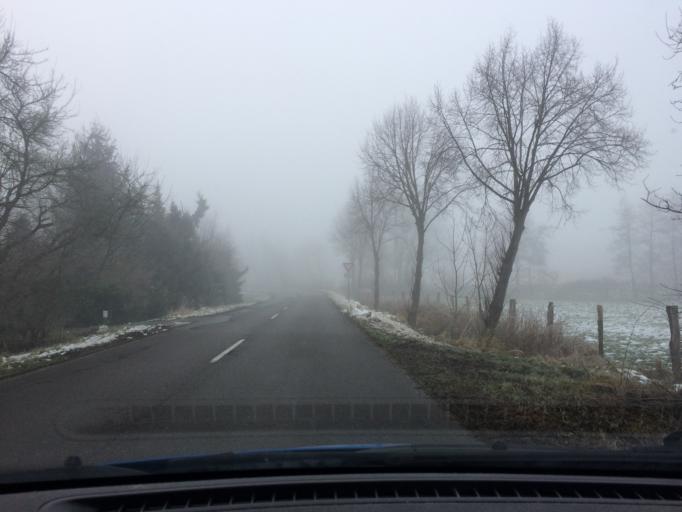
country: DE
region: Schleswig-Holstein
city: Kollow
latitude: 53.4576
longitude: 10.4627
